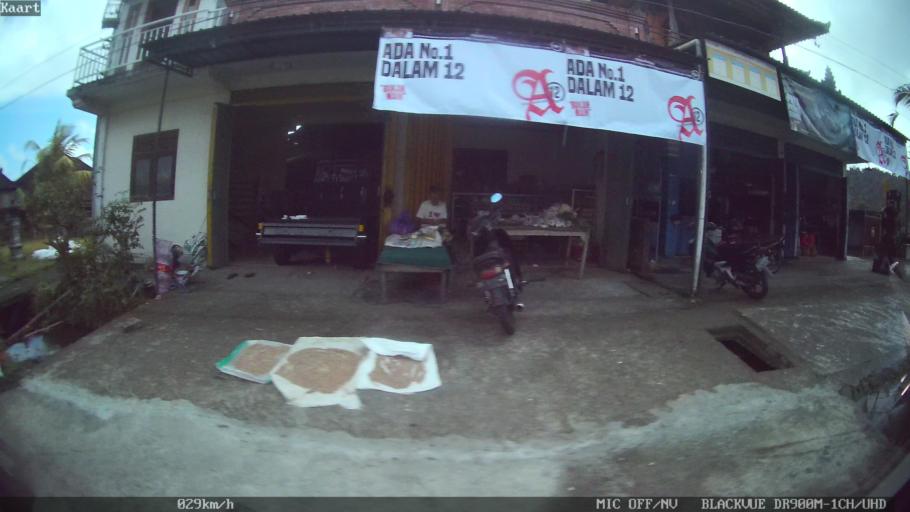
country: ID
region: Bali
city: Banjar Abuan
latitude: -8.4584
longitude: 115.3400
